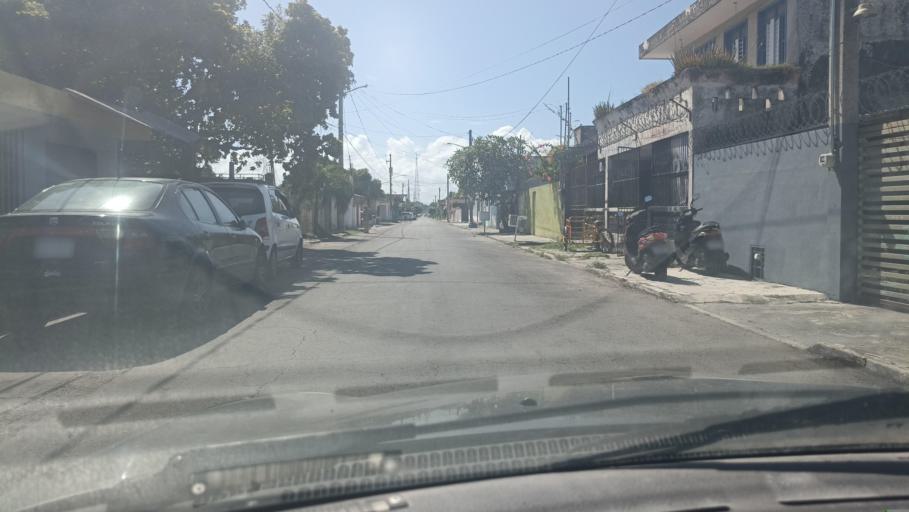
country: MX
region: Quintana Roo
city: Chetumal
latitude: 18.5136
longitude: -88.2868
